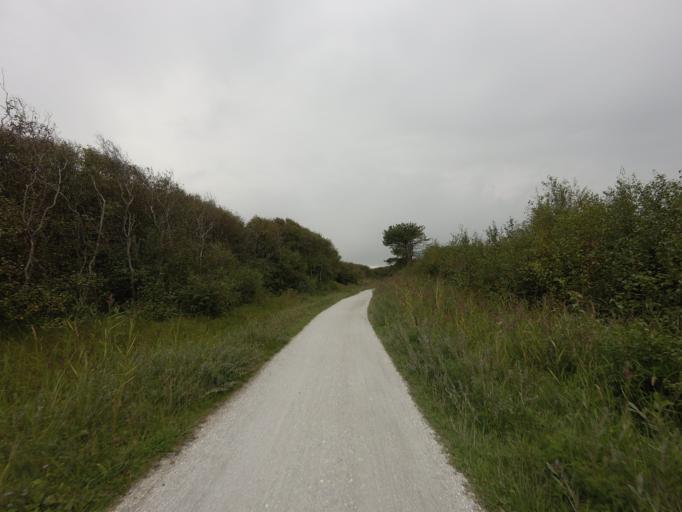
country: NL
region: Friesland
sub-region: Gemeente Schiermonnikoog
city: Schiermonnikoog
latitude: 53.4954
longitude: 6.1737
